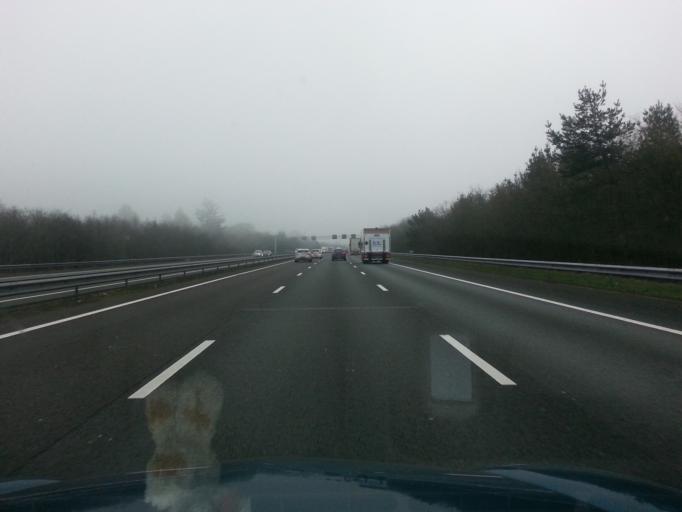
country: NL
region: Gelderland
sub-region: Gemeente Arnhem
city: Hoogkamp
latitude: 52.0271
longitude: 5.8672
